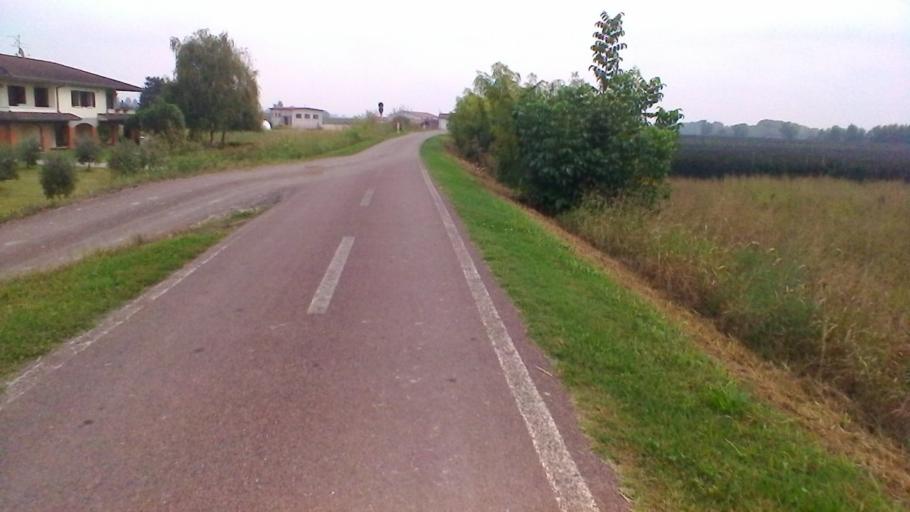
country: IT
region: Veneto
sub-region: Provincia di Verona
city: Zevio
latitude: 45.3860
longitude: 11.0975
